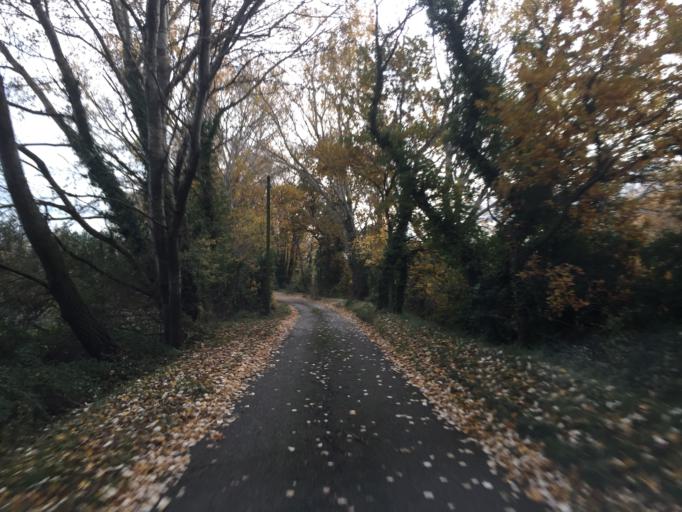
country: FR
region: Provence-Alpes-Cote d'Azur
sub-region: Departement du Vaucluse
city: Sarrians
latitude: 44.0667
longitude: 4.9320
